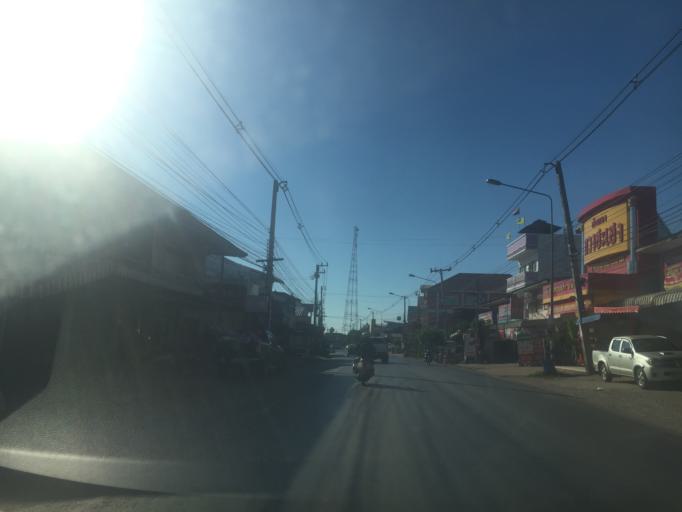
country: TH
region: Changwat Udon Thani
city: Si That
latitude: 16.9747
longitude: 103.2143
